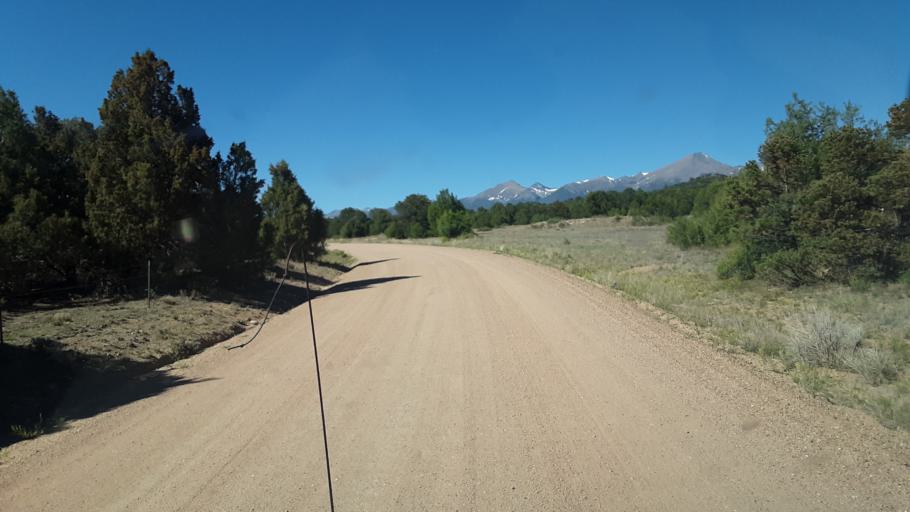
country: US
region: Colorado
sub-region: Custer County
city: Westcliffe
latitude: 38.2679
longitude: -105.5461
